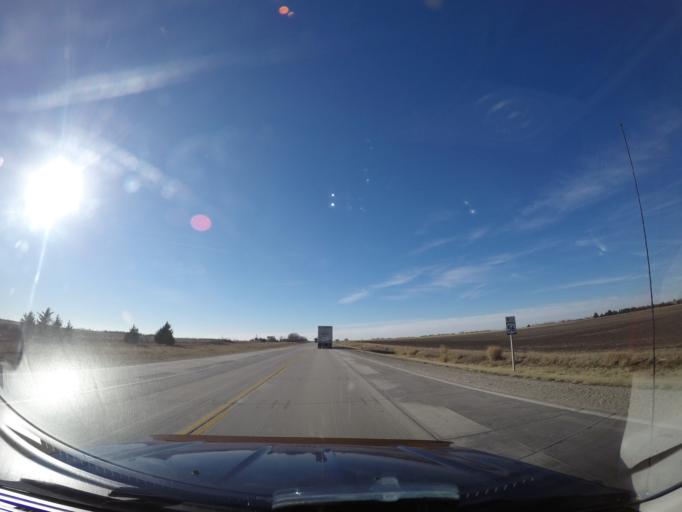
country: US
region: Kansas
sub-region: Marion County
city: Marion
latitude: 38.3558
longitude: -97.0956
